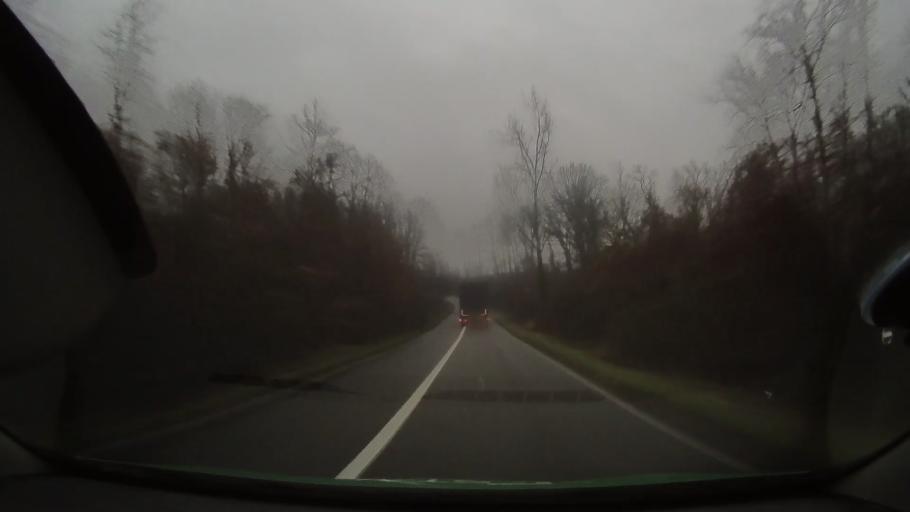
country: RO
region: Arad
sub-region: Comuna Beliu
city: Beliu
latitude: 46.5121
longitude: 21.9612
